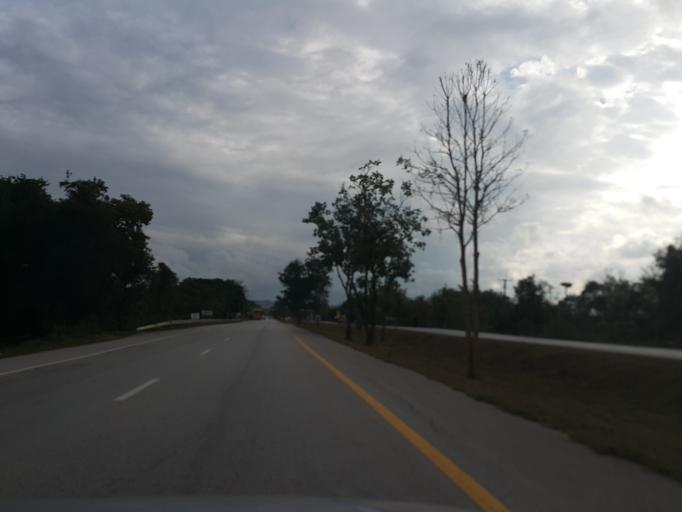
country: TH
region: Lampang
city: Ko Kha
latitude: 18.1682
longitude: 99.4061
